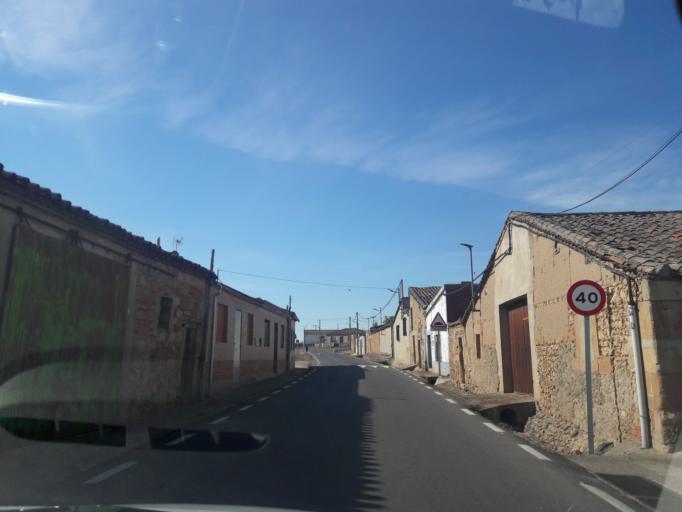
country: ES
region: Castille and Leon
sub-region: Provincia de Salamanca
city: Espino de la Orbada
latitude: 41.1068
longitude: -5.4226
